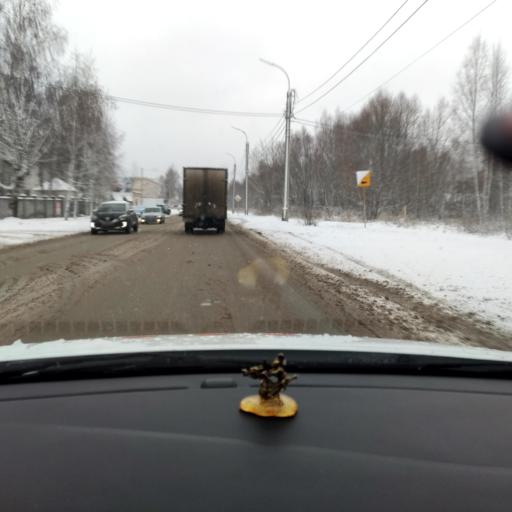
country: RU
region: Tatarstan
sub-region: Zelenodol'skiy Rayon
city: Zelenodolsk
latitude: 55.8633
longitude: 48.5493
